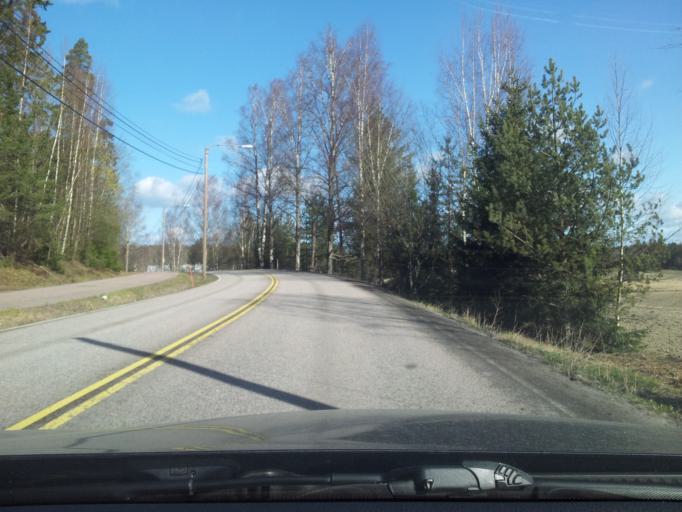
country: FI
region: Uusimaa
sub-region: Helsinki
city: Espoo
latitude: 60.1854
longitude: 24.6694
